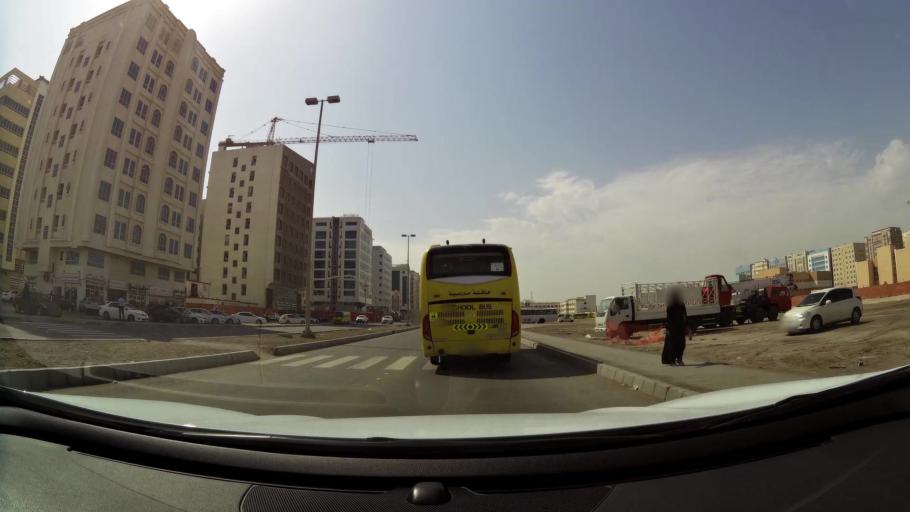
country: AE
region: Abu Dhabi
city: Abu Dhabi
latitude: 24.3380
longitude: 54.5345
